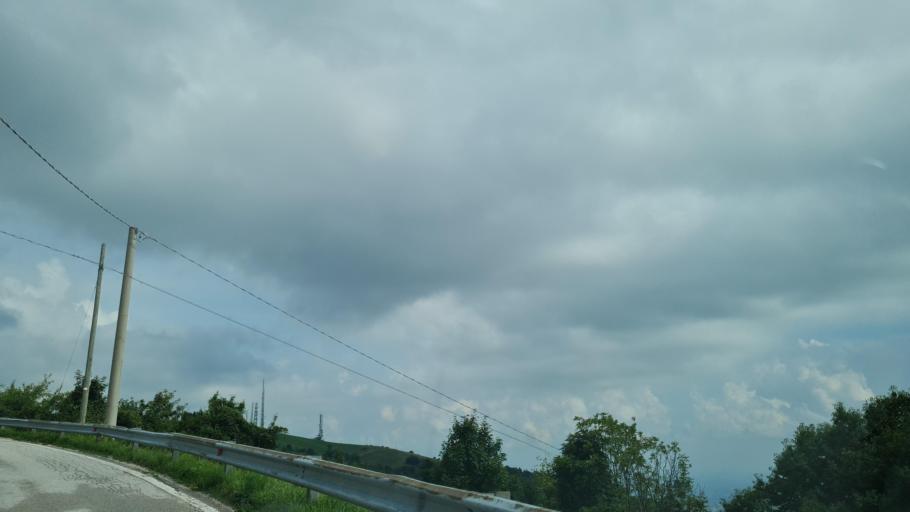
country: IT
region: Veneto
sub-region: Provincia di Vicenza
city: San Nazario
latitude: 45.8028
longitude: 11.6586
